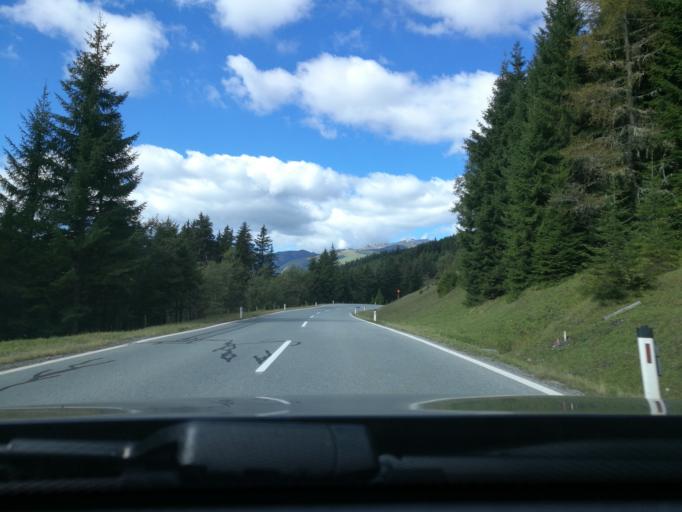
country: AT
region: Salzburg
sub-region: Politischer Bezirk Zell am See
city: Krimml
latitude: 47.2434
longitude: 12.1035
